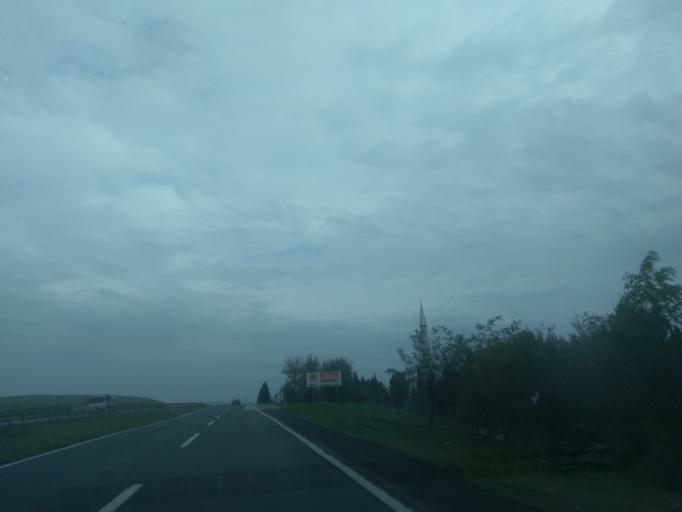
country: TR
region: Istanbul
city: Silivri
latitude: 41.0769
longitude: 28.1753
